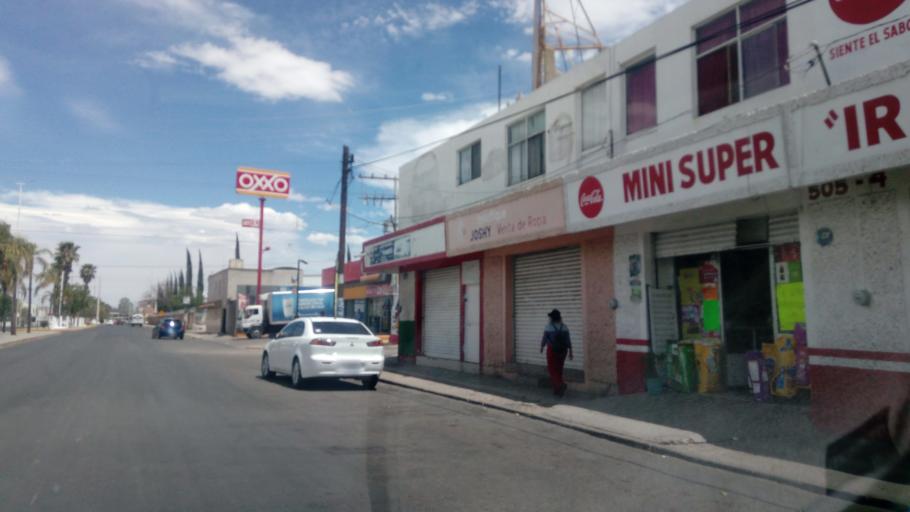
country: MX
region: Durango
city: Victoria de Durango
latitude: 23.9964
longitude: -104.6686
